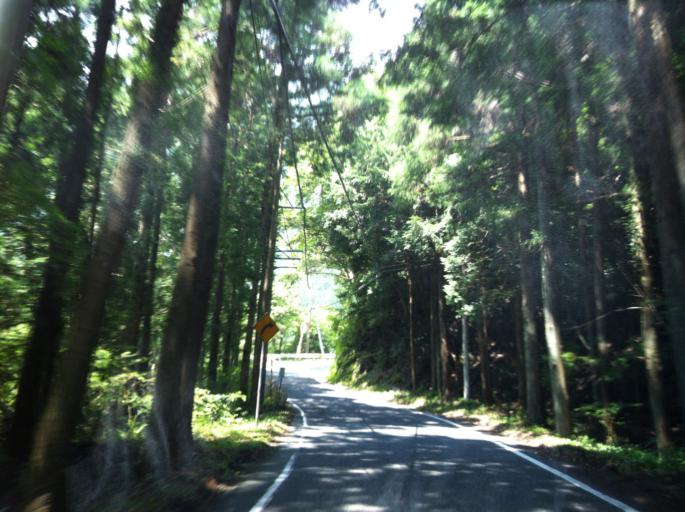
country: JP
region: Shizuoka
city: Shizuoka-shi
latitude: 35.2586
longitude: 138.3288
